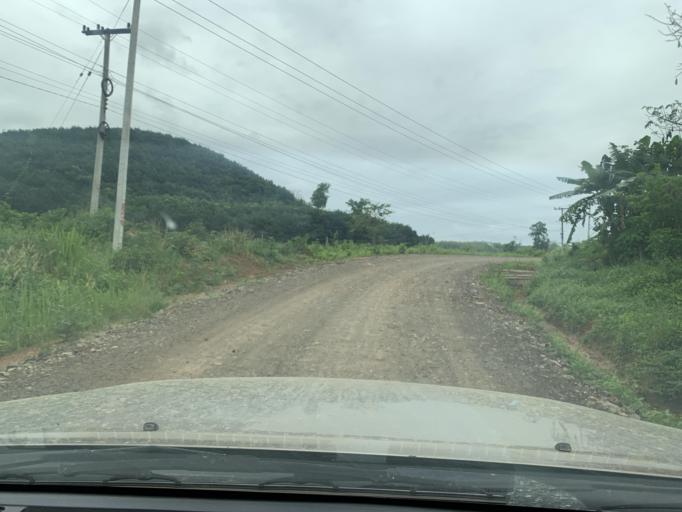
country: TH
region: Nan
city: Mae Charim
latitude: 18.4169
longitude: 101.4573
